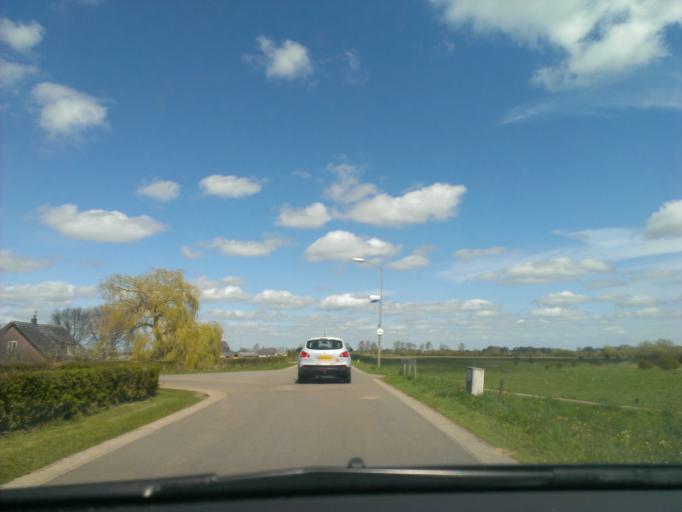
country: NL
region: Overijssel
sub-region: Gemeente Olst-Wijhe
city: Wijhe
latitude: 52.3823
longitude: 6.1143
